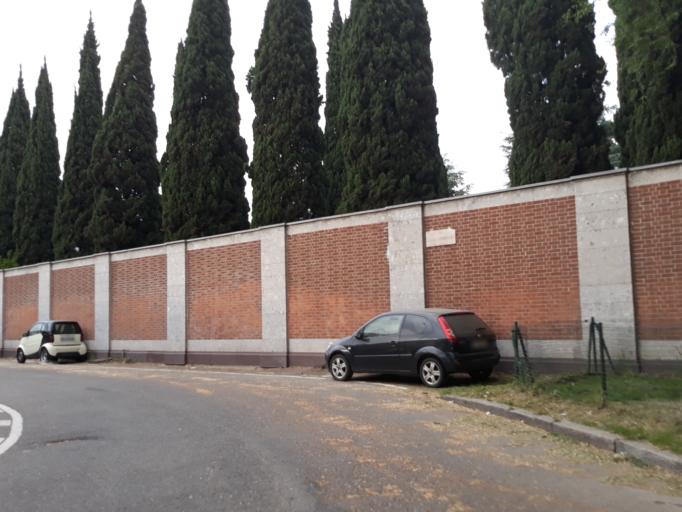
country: IT
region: Lombardy
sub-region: Citta metropolitana di Milano
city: Milano
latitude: 45.4880
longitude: 9.1742
